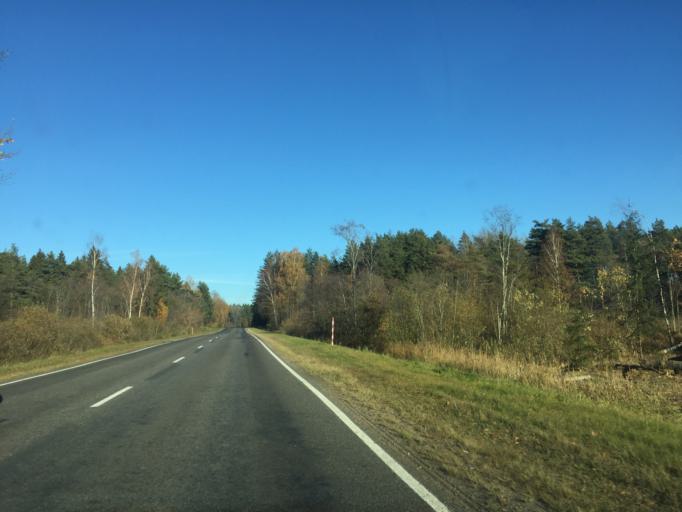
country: BY
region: Vitebsk
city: Dzisna
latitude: 55.3657
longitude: 28.3618
